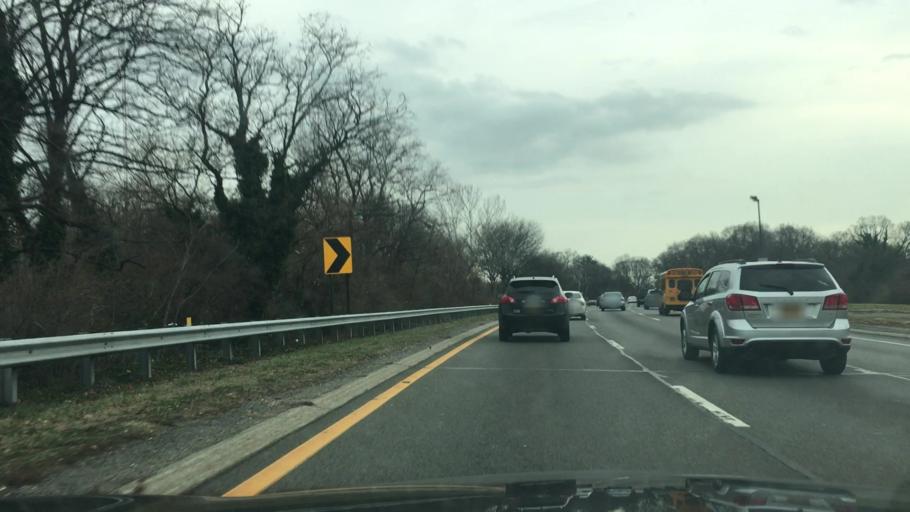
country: US
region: New York
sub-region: Nassau County
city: South Hempstead
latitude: 40.6863
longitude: -73.6133
